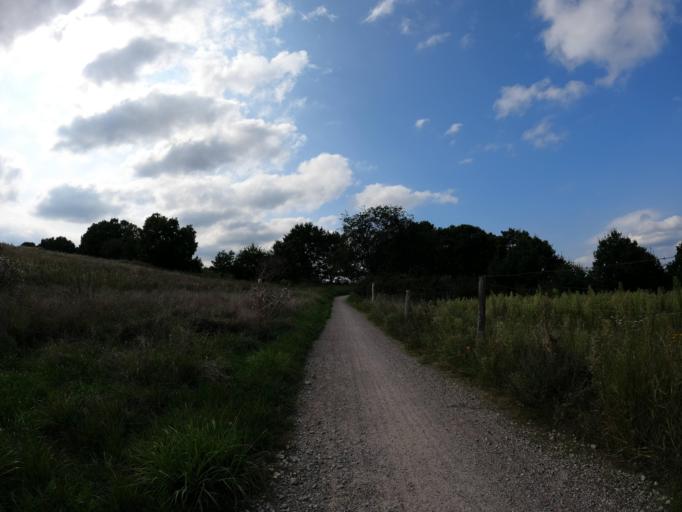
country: DE
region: Mecklenburg-Vorpommern
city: Malchow
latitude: 53.4960
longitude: 12.4307
